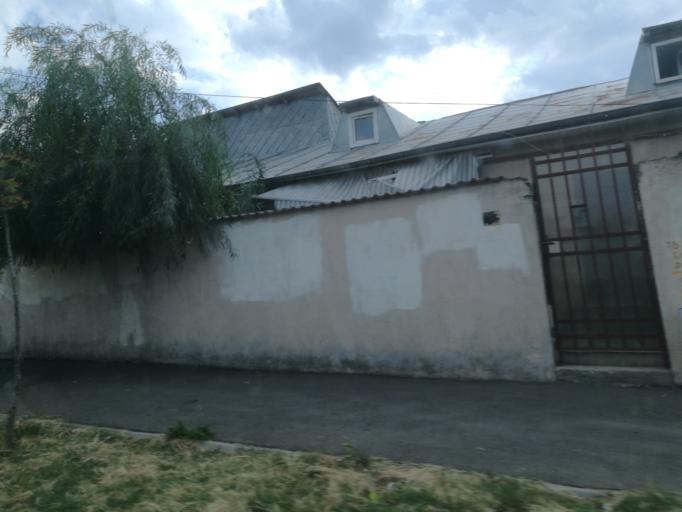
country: RO
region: Ilfov
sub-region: Comuna Mogosoaia
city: Mogosoaia
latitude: 44.5009
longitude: 26.0266
